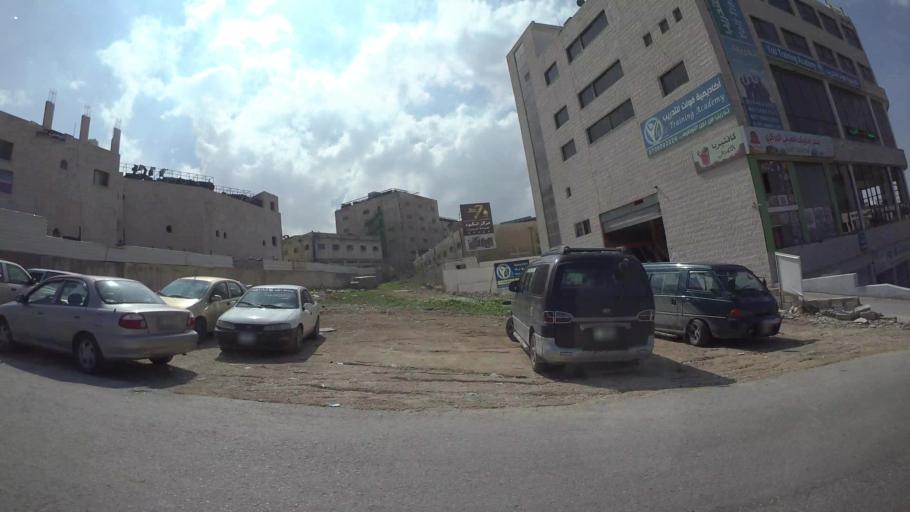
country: JO
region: Zarqa
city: Russeifa
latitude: 31.9985
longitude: 36.0029
